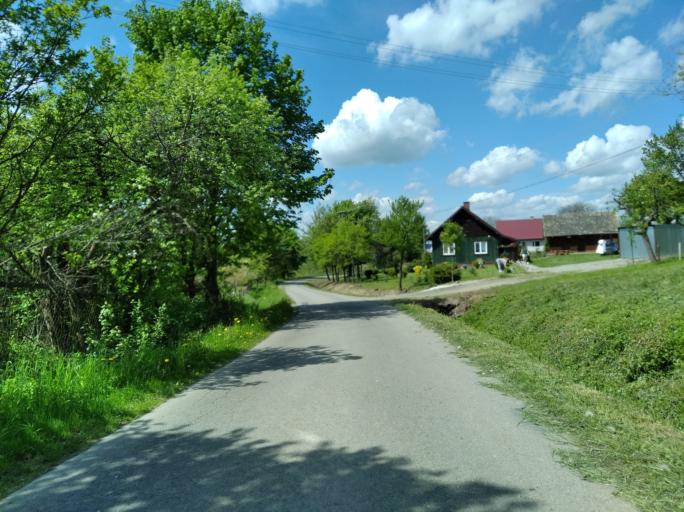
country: PL
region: Subcarpathian Voivodeship
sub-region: Powiat jasielski
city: Kolaczyce
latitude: 49.8418
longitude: 21.4663
